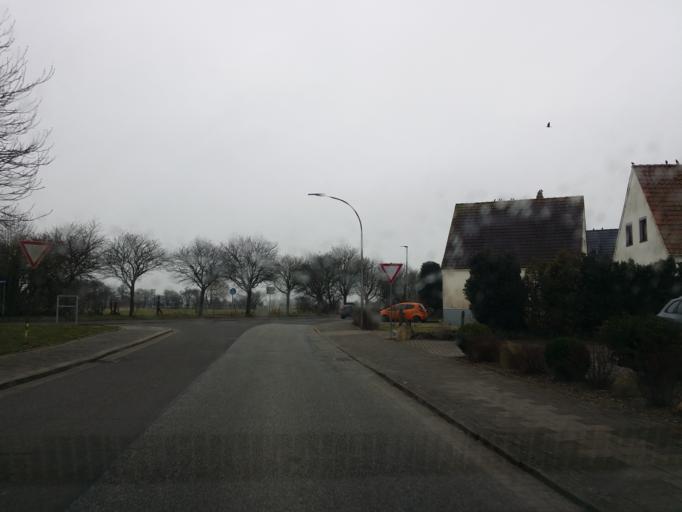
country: DE
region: Schleswig-Holstein
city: Burg auf Fehmarn
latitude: 54.4317
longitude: 11.2002
